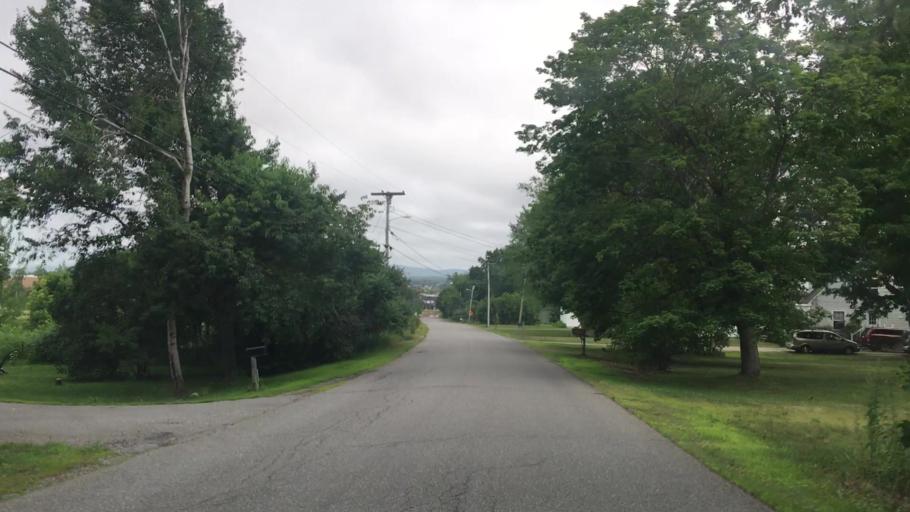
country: US
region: Maine
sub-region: Penobscot County
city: Veazie
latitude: 44.8452
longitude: -68.7464
